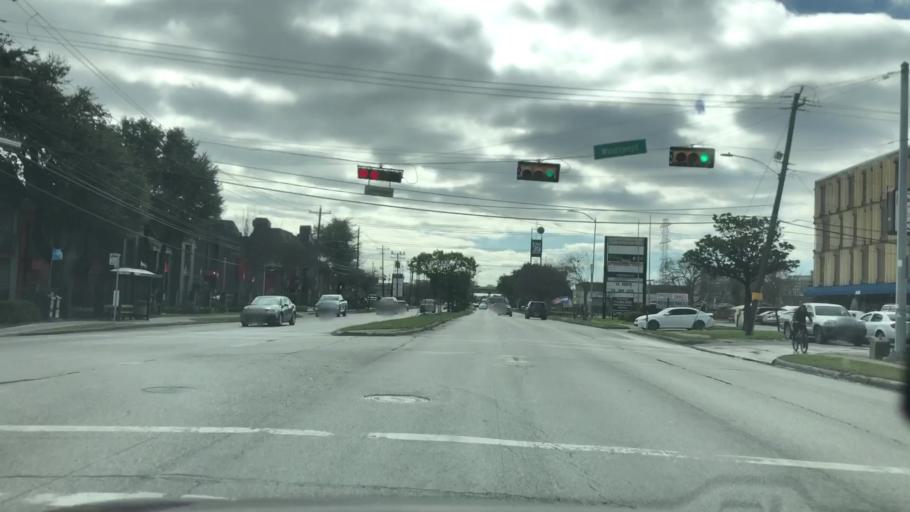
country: US
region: Texas
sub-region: Harris County
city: Piney Point Village
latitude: 29.7258
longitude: -95.5012
